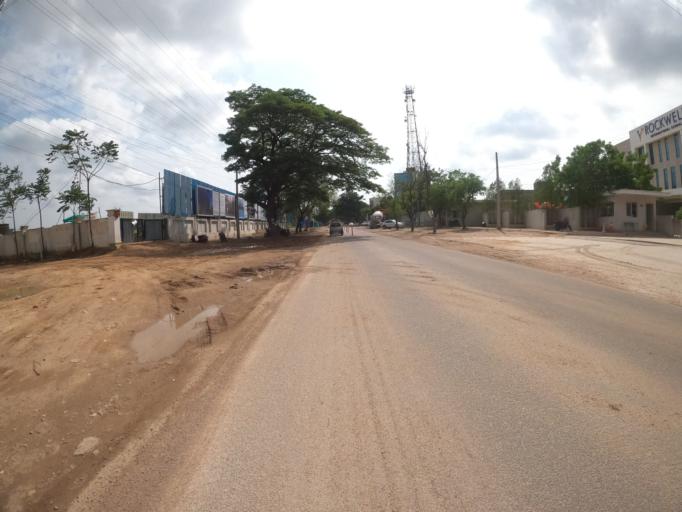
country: IN
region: Telangana
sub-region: Medak
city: Serilingampalle
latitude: 17.3860
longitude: 78.3349
